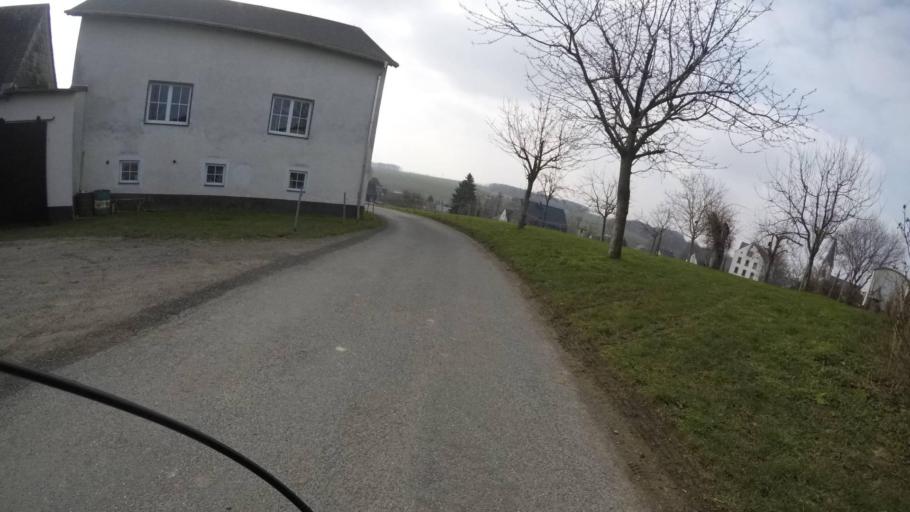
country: DE
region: Saxony
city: Niederfrohna
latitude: 50.8726
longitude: 12.6956
